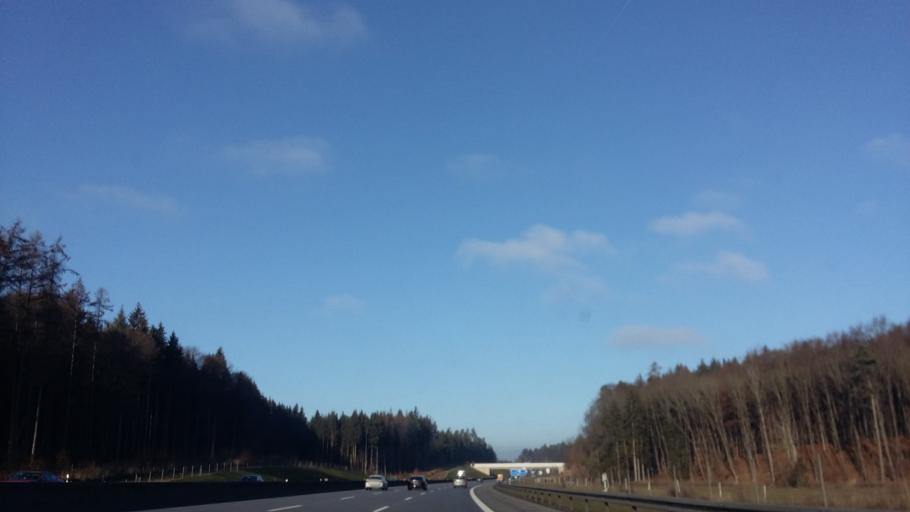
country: DE
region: Bavaria
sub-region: Swabia
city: Adelzhausen
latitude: 48.3309
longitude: 11.1658
